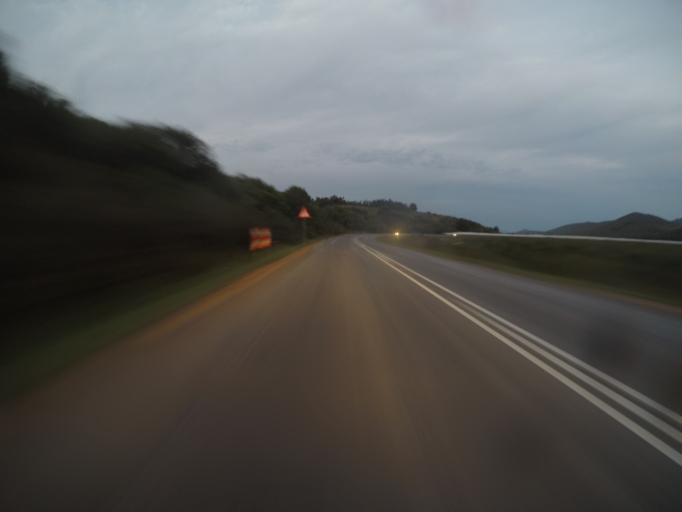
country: ZA
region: Western Cape
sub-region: Eden District Municipality
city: Plettenberg Bay
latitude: -33.8108
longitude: 23.7447
